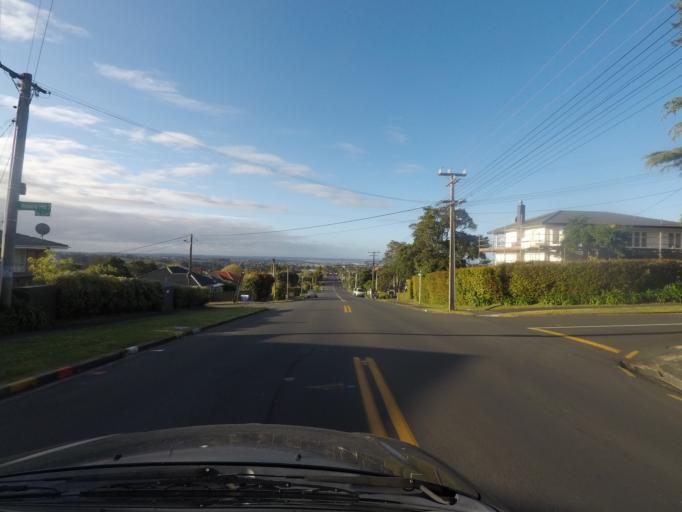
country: NZ
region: Auckland
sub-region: Auckland
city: Waitakere
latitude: -36.9172
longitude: 174.6578
